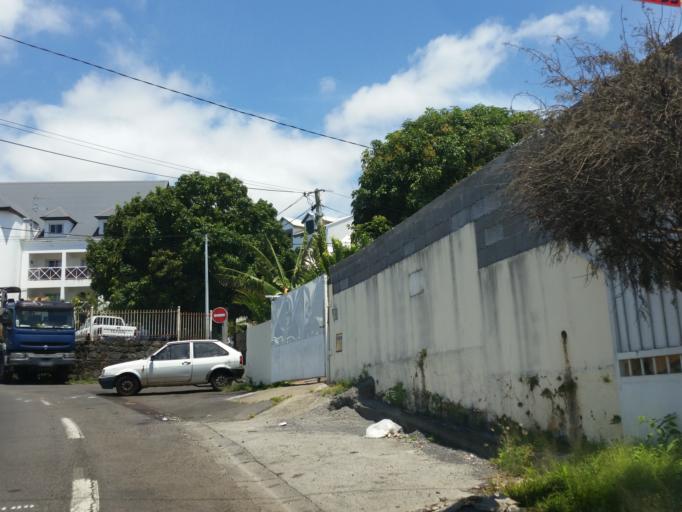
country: RE
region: Reunion
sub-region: Reunion
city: Saint-Denis
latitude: -20.9110
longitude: 55.4853
